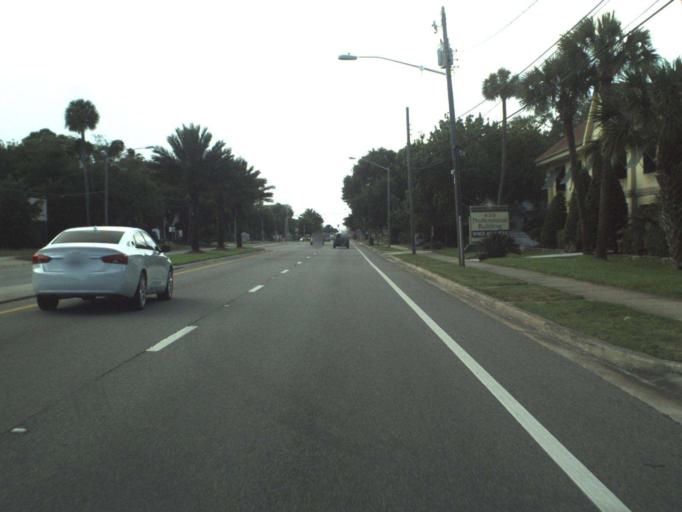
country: US
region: Florida
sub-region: Volusia County
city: Daytona Beach
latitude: 29.2037
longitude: -81.0189
